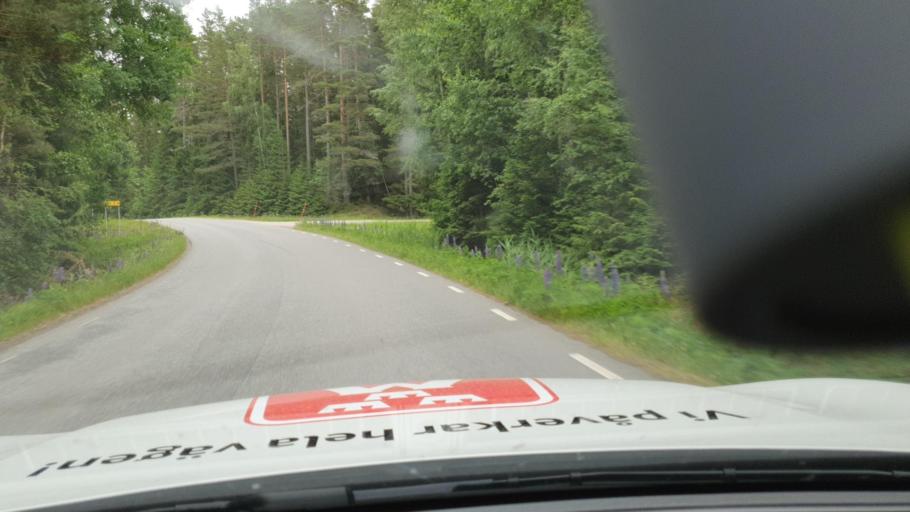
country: SE
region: Vaestra Goetaland
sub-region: Karlsborgs Kommun
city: Karlsborg
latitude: 58.6628
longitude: 14.4192
